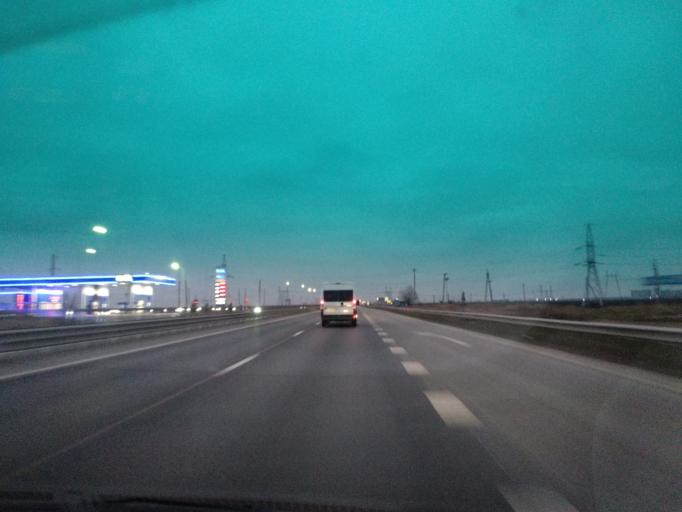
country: RU
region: Adygeya
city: Adygeysk
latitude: 44.8587
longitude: 39.1968
